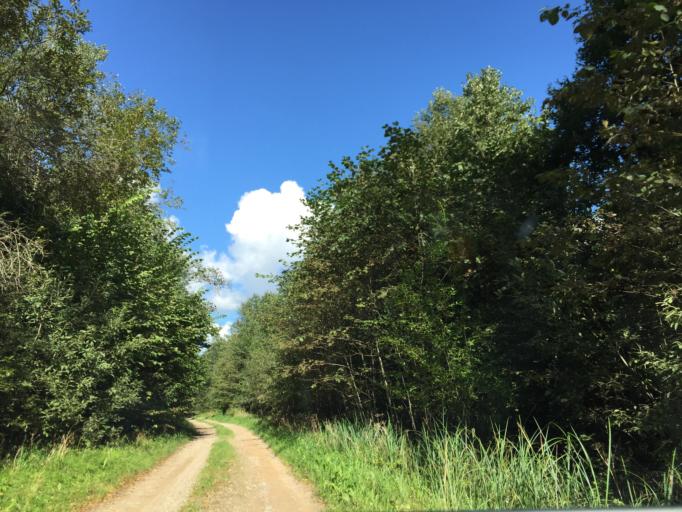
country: LV
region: Kuldigas Rajons
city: Kuldiga
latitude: 56.9774
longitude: 21.9087
